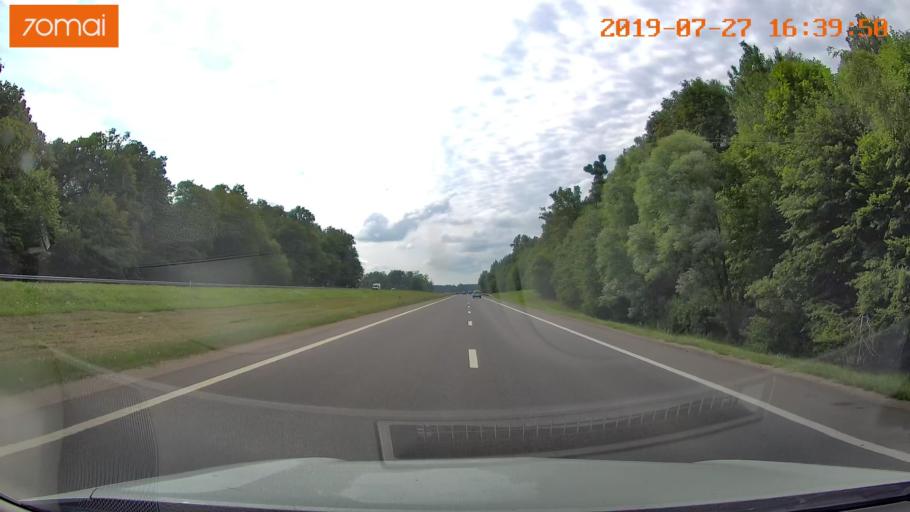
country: RU
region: Kaliningrad
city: Gvardeysk
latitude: 54.6496
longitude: 21.1896
